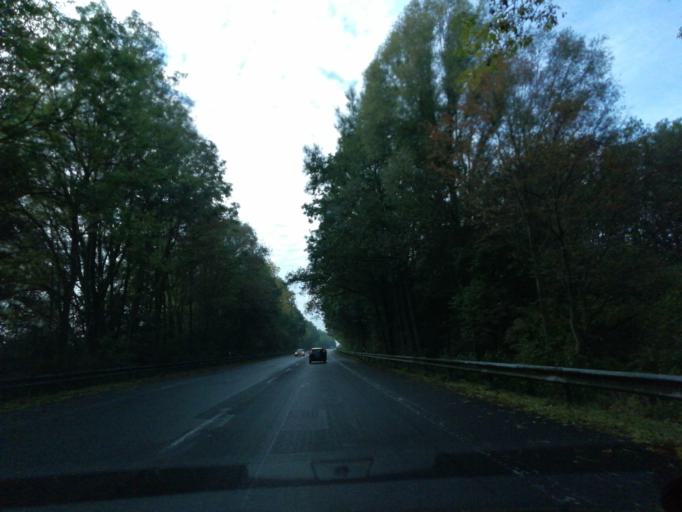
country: DE
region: Lower Saxony
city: Fedderwarden
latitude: 53.5618
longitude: 8.0526
